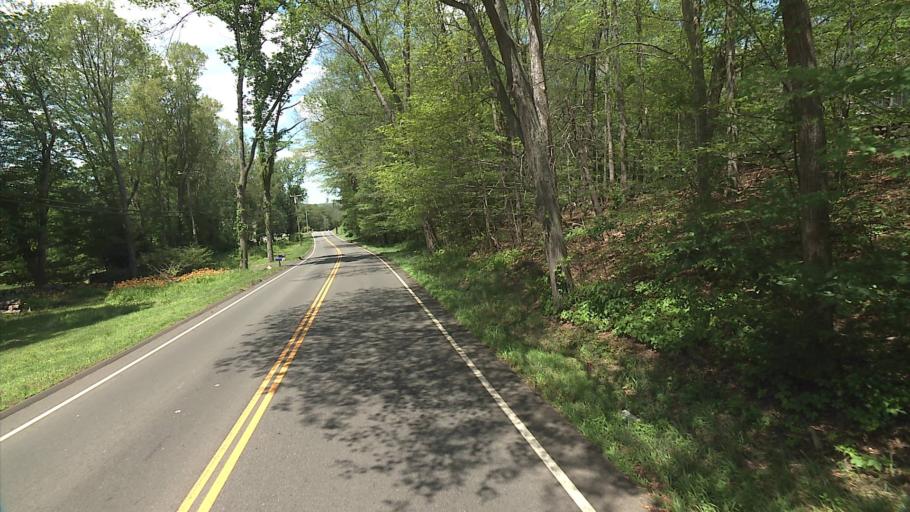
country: US
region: Connecticut
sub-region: Middlesex County
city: Moodus
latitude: 41.4879
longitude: -72.4470
